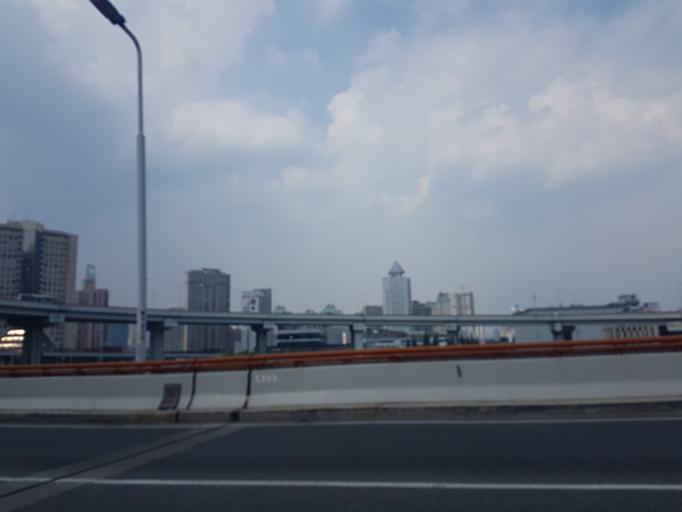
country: CN
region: Shanghai Shi
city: Luwan
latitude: 31.2096
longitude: 121.4967
